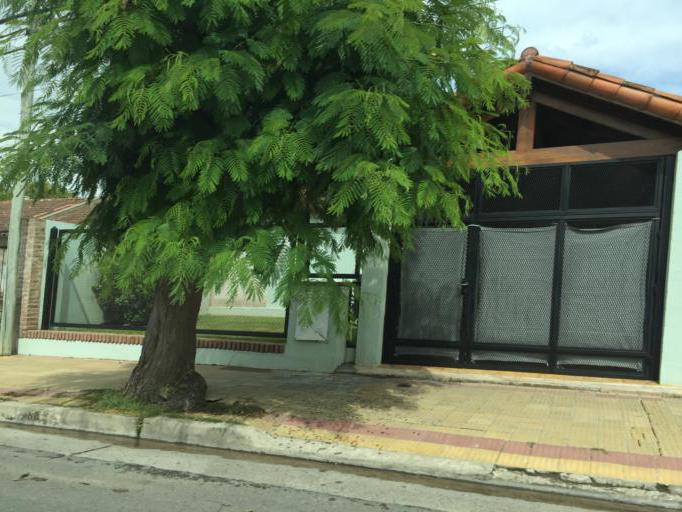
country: AR
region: Buenos Aires
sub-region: Partido de Tandil
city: Tandil
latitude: -37.3227
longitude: -59.1091
